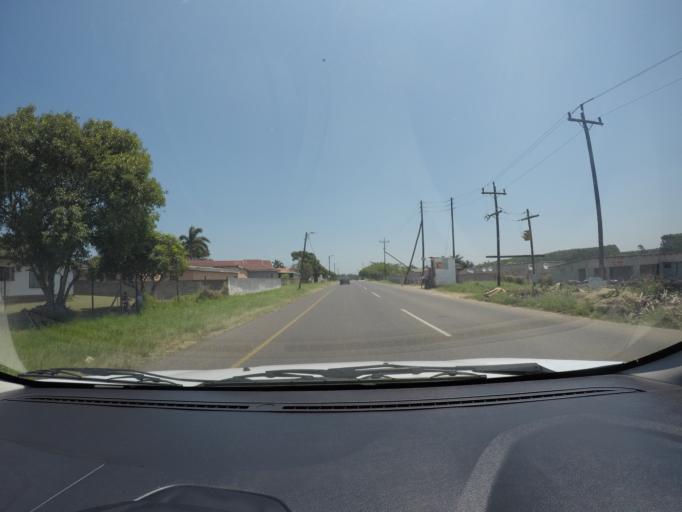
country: ZA
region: KwaZulu-Natal
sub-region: uThungulu District Municipality
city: eSikhawini
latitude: -28.8861
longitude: 31.8848
